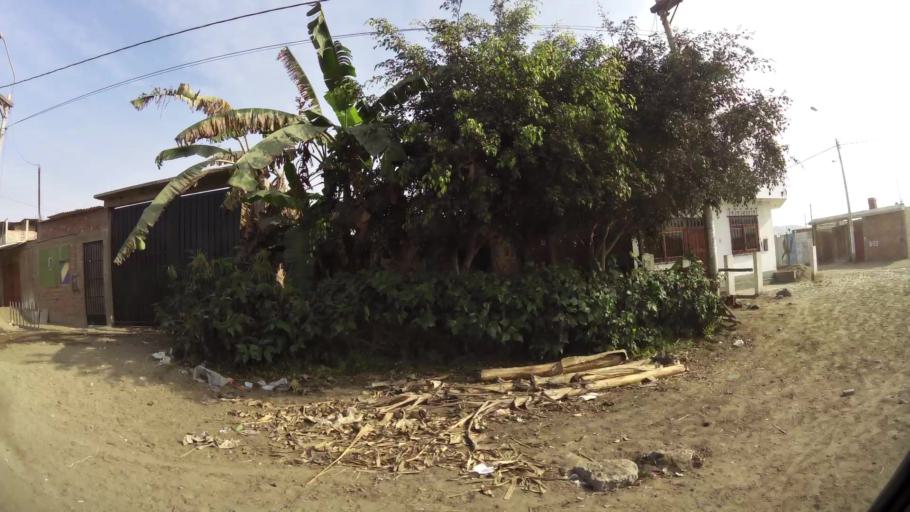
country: PE
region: Lima
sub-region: Lima
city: Santa Rosa
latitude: -11.7621
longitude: -77.1670
